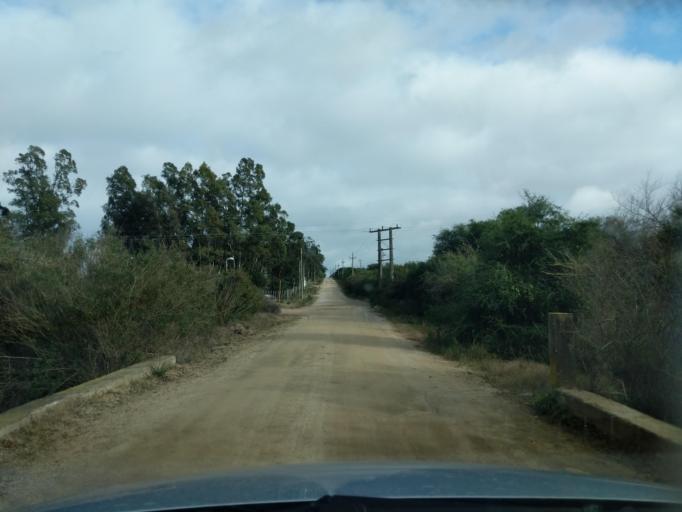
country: UY
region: Florida
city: Florida
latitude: -34.0591
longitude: -56.2152
